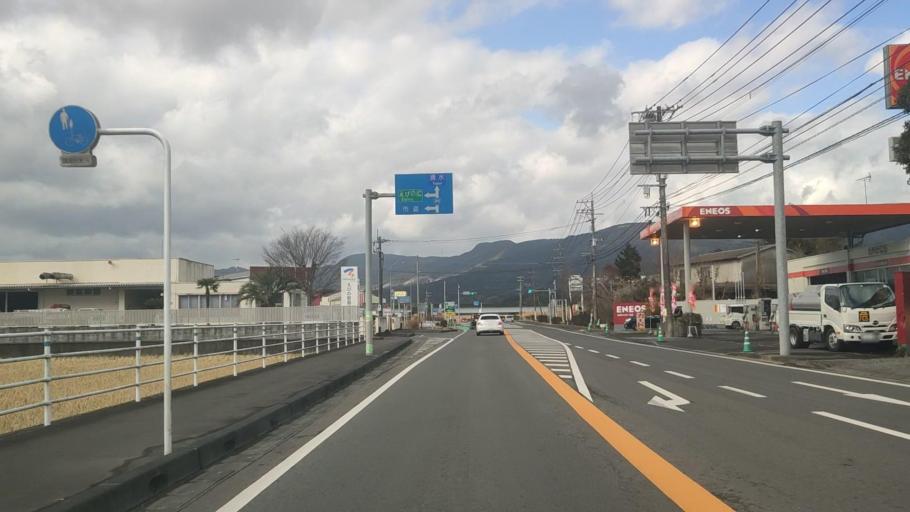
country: JP
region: Kumamoto
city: Hitoyoshi
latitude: 32.0512
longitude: 130.8056
